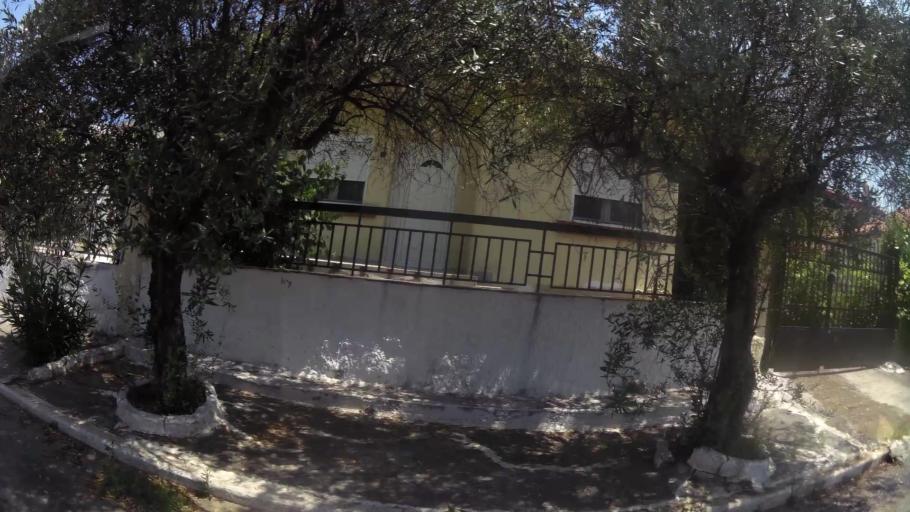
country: GR
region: Central Macedonia
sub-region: Nomos Thessalonikis
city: Nea Michaniona
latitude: 40.4766
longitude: 22.8699
